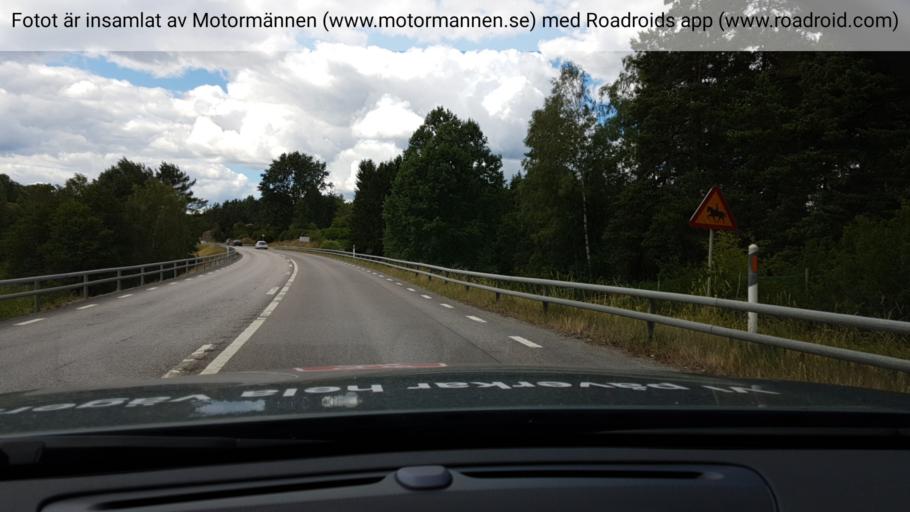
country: SE
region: Stockholm
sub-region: Osterakers Kommun
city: Akersberga
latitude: 59.4271
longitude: 18.2623
